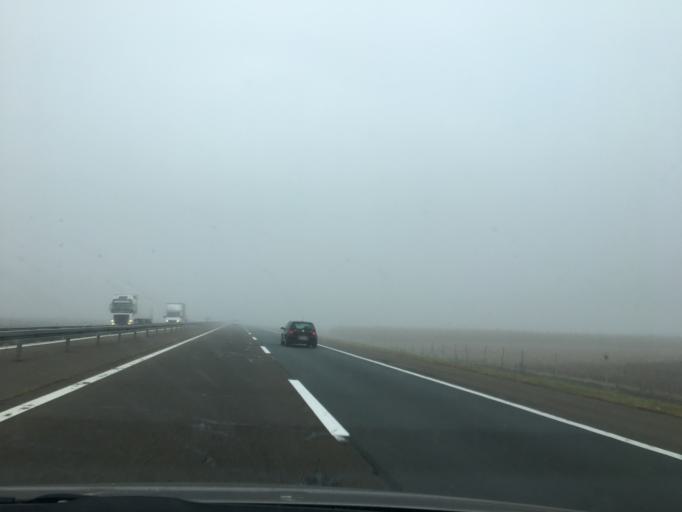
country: RS
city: Novi Banovci
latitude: 44.9593
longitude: 20.2530
